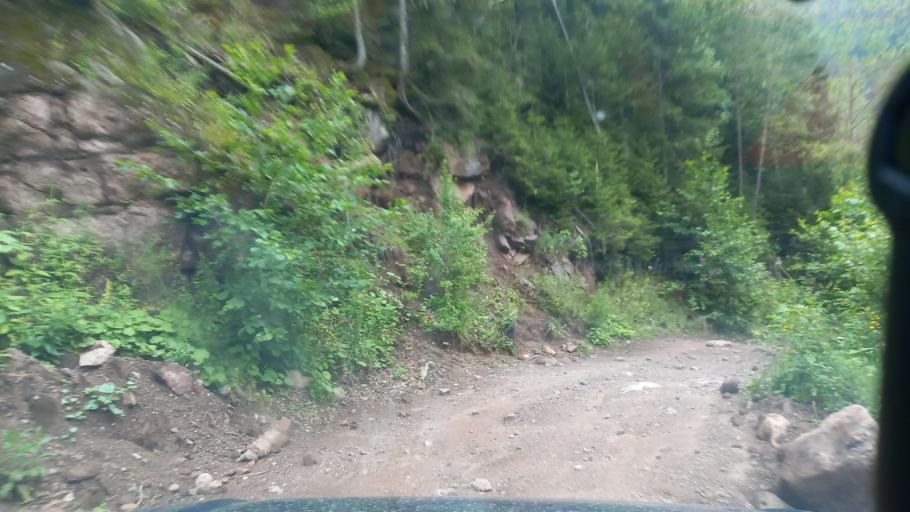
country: RU
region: Karachayevo-Cherkesiya
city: Kurdzhinovo
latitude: 43.8157
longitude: 40.8891
